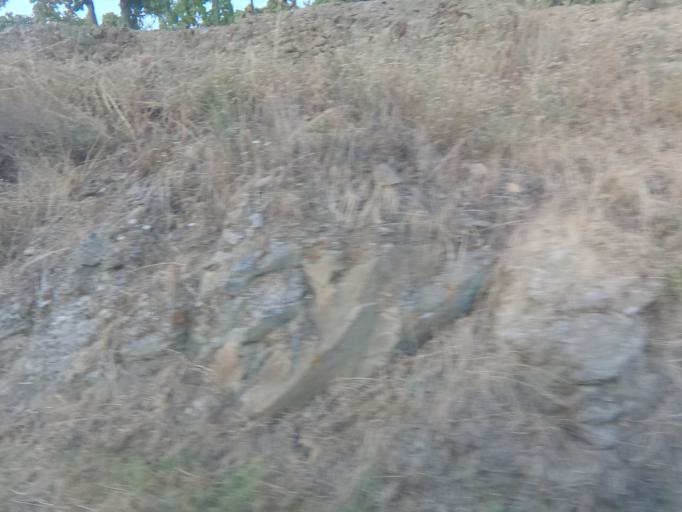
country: PT
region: Viseu
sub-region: Armamar
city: Armamar
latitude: 41.1680
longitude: -7.6855
